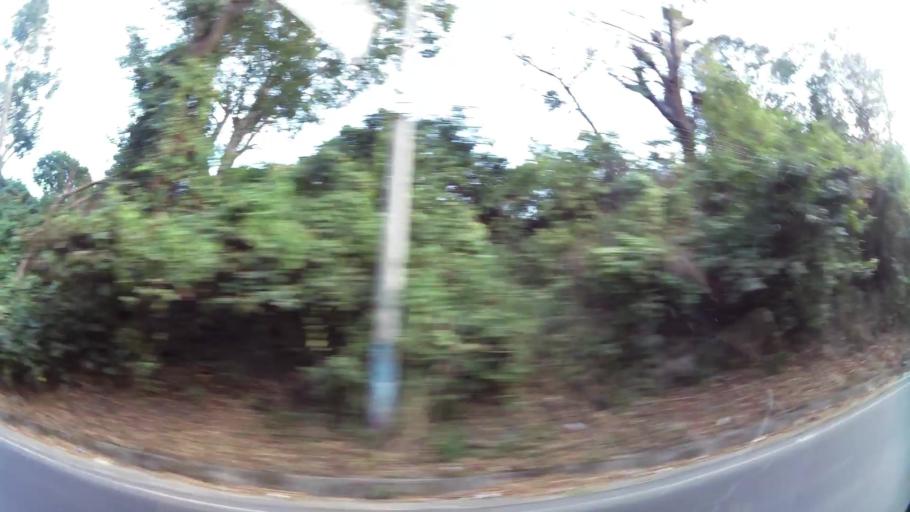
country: SV
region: San Vicente
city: Apastepeque
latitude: 13.6610
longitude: -88.7954
